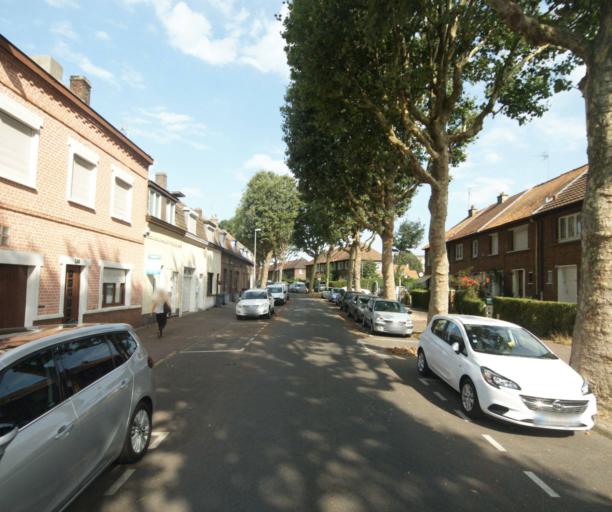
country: FR
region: Nord-Pas-de-Calais
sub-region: Departement du Nord
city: Tourcoing
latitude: 50.7338
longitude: 3.1782
